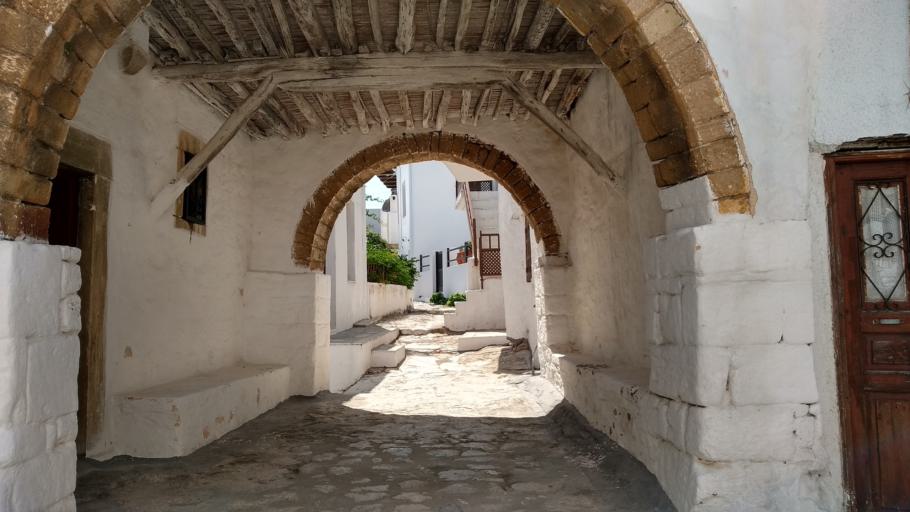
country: GR
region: Central Greece
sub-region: Nomos Evvoias
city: Skyros
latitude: 38.9073
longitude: 24.5678
